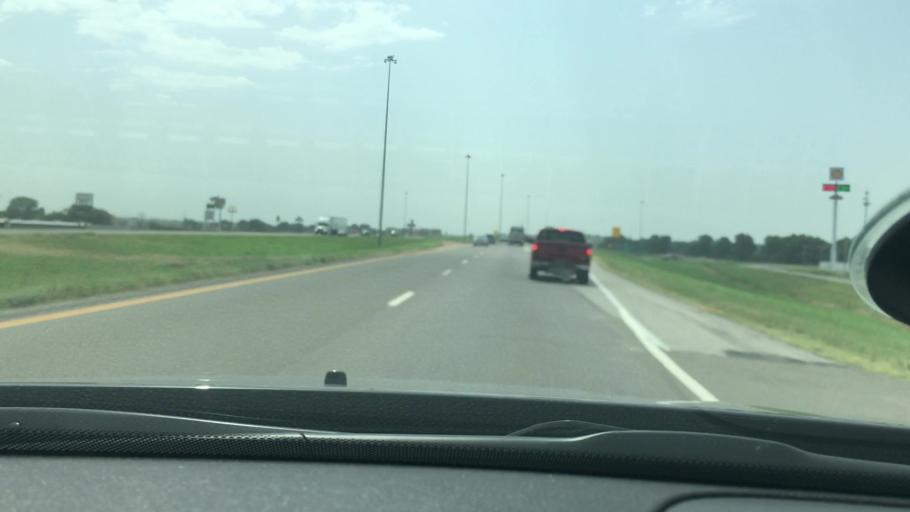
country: US
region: Oklahoma
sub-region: Garvin County
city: Pauls Valley
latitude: 34.7436
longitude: -97.2672
